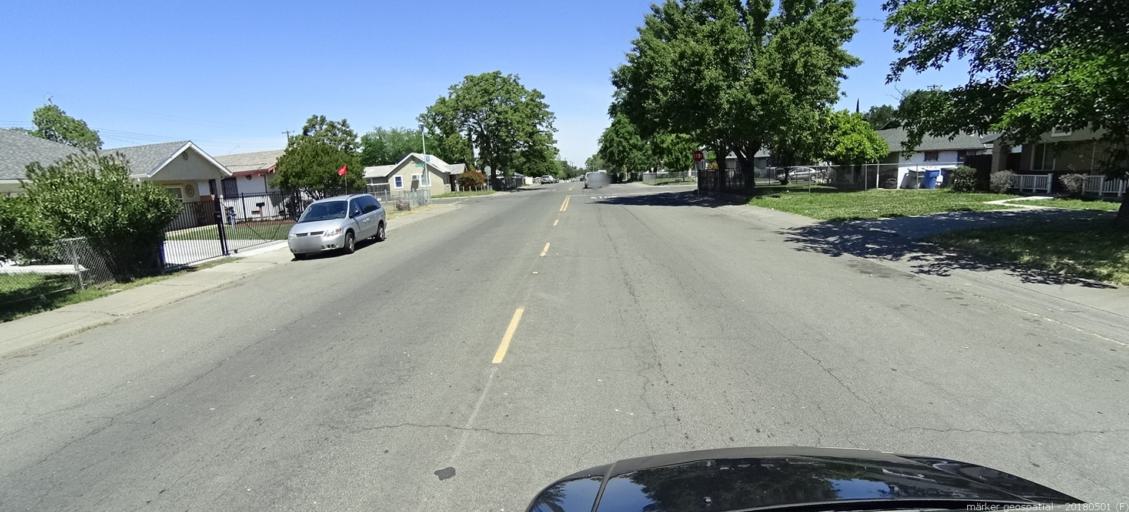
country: US
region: California
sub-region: Sacramento County
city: Rio Linda
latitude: 38.6379
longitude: -121.4385
